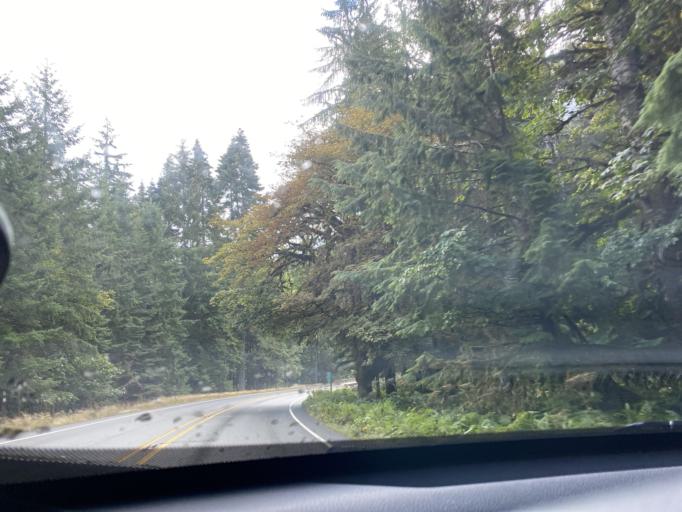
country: CA
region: British Columbia
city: Sooke
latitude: 48.0573
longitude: -123.7885
